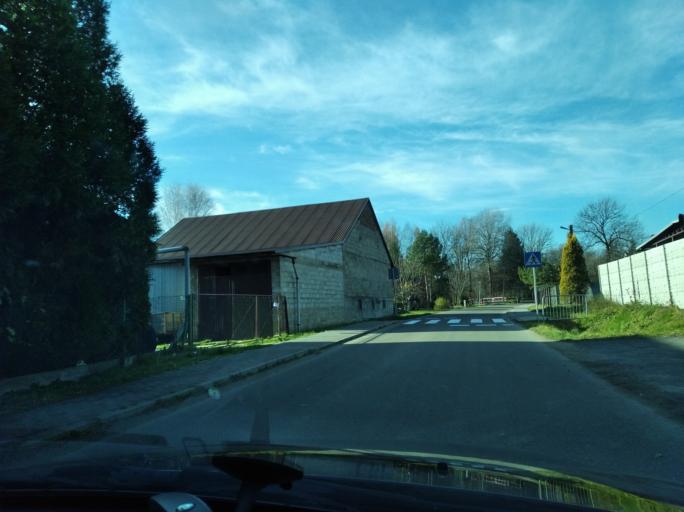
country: PL
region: Subcarpathian Voivodeship
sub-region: Powiat rzeszowski
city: Lutoryz
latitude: 49.9671
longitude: 21.9096
